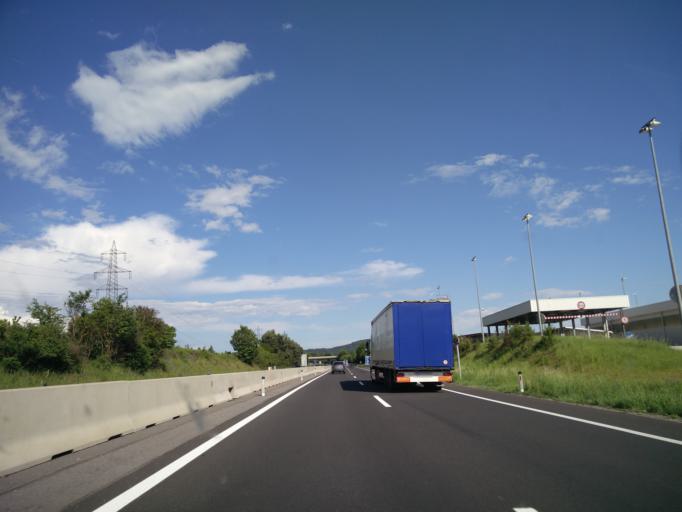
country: AT
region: Carinthia
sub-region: Politischer Bezirk Volkermarkt
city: Voelkermarkt
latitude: 46.6848
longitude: 14.6592
